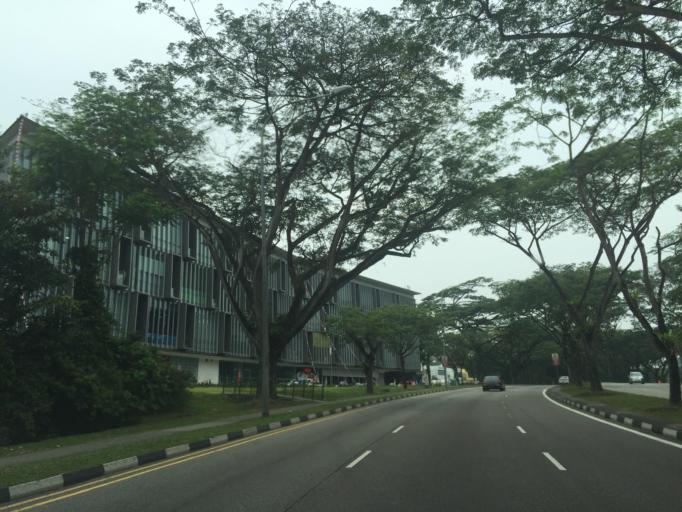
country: SG
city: Singapore
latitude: 1.3842
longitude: 103.8248
